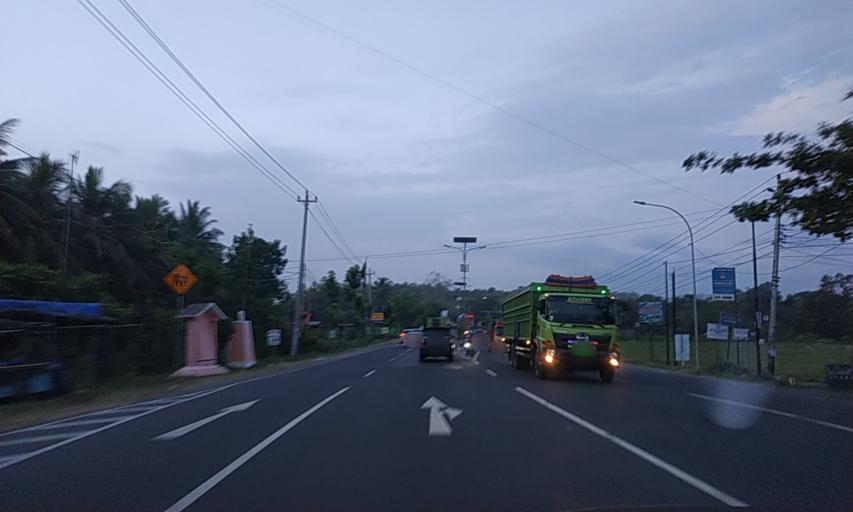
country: ID
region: Daerah Istimewa Yogyakarta
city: Srandakan
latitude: -7.8596
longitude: 110.2120
